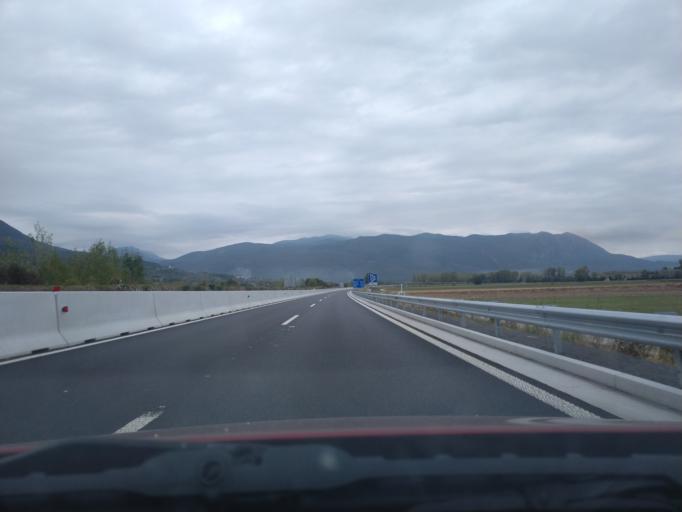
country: SI
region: Ajdovscina
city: Ajdovscina
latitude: 45.8775
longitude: 13.9117
